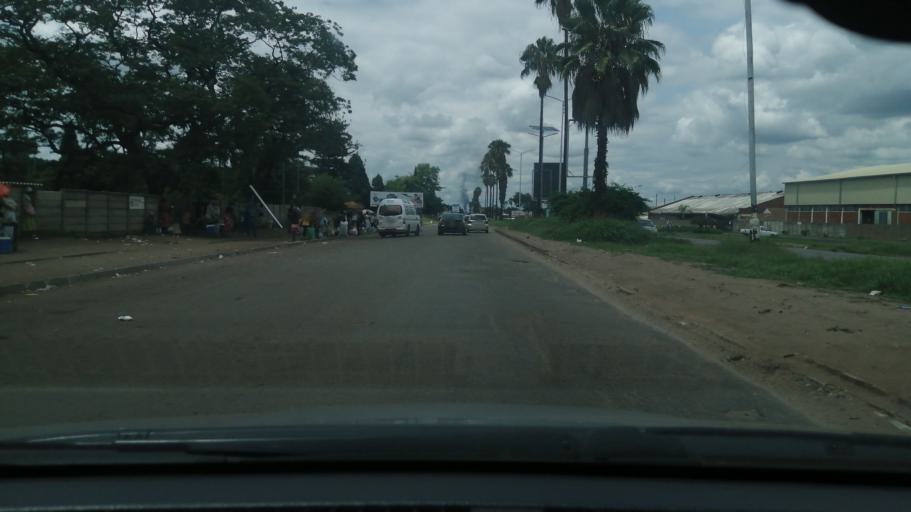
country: ZW
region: Harare
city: Harare
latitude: -17.8573
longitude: 31.0302
